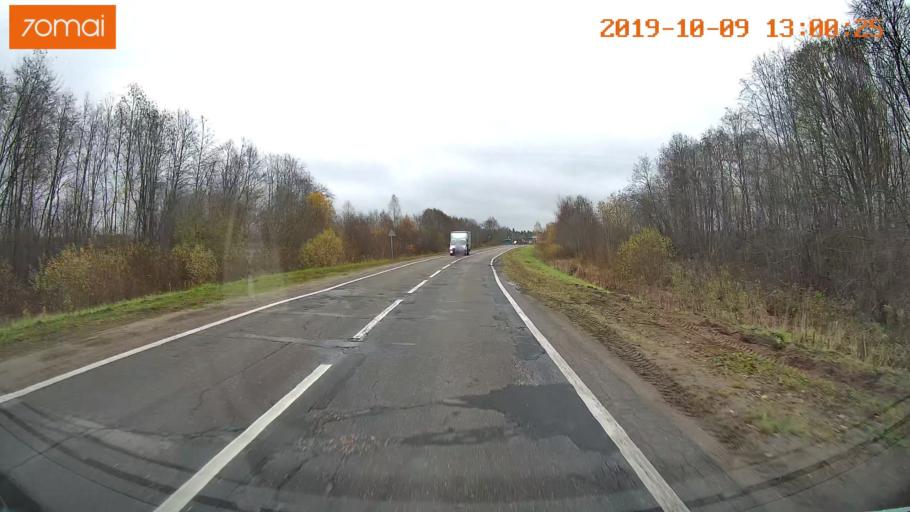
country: RU
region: Jaroslavl
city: Prechistoye
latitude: 58.3775
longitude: 40.4797
